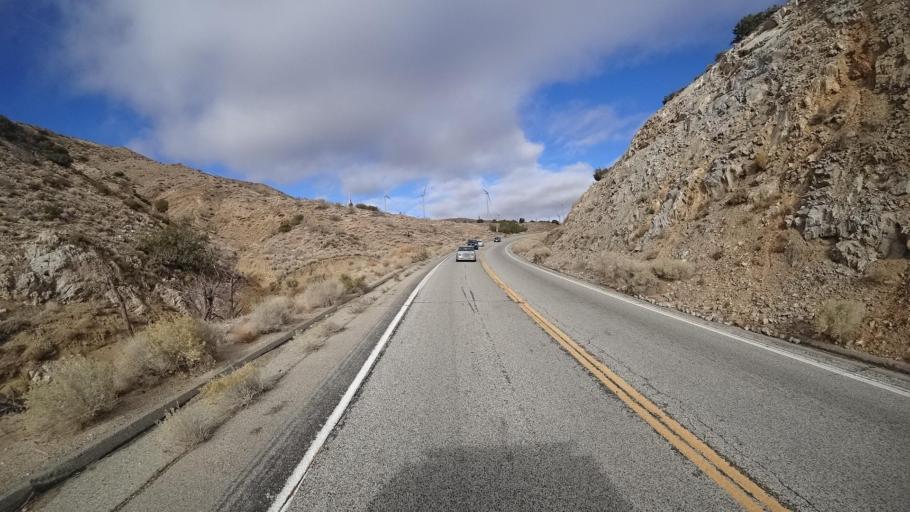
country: US
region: California
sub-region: Kern County
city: Tehachapi
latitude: 35.0161
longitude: -118.3488
